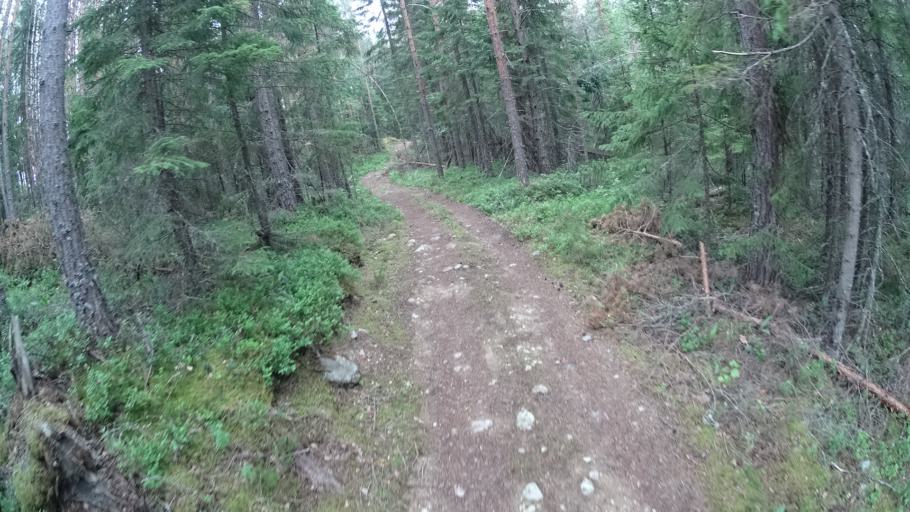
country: FI
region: Southern Savonia
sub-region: Mikkeli
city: Maentyharju
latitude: 61.1842
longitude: 26.8915
